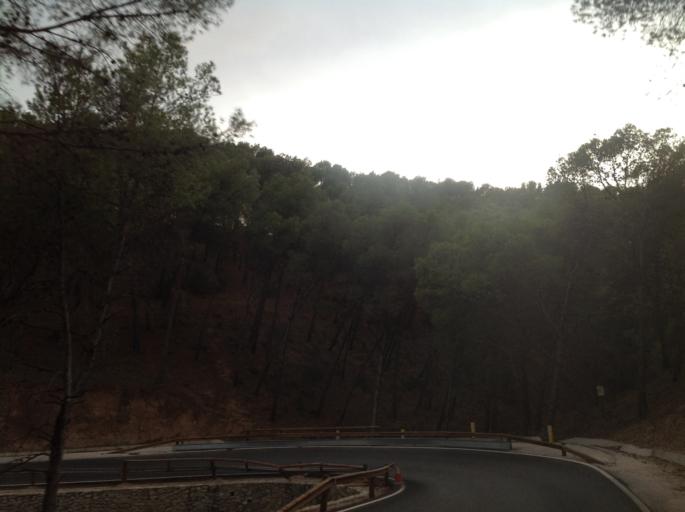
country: ES
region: Andalusia
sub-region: Provincia de Malaga
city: Ardales
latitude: 36.9111
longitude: -4.7990
